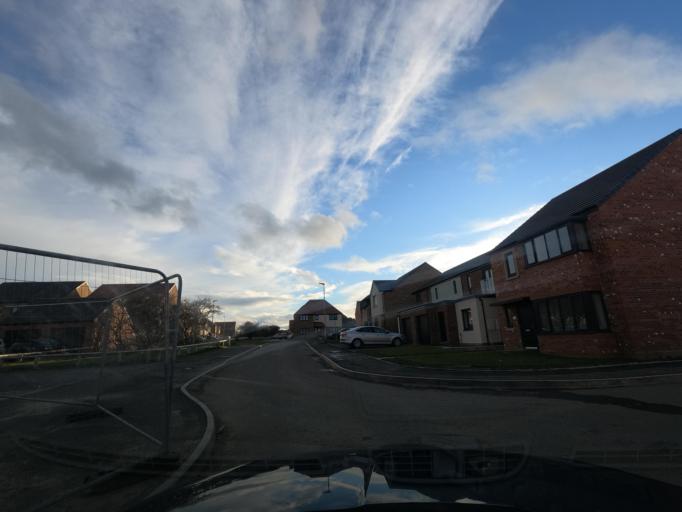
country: GB
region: England
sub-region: Northumberland
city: Cramlington
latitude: 55.0917
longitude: -1.5919
